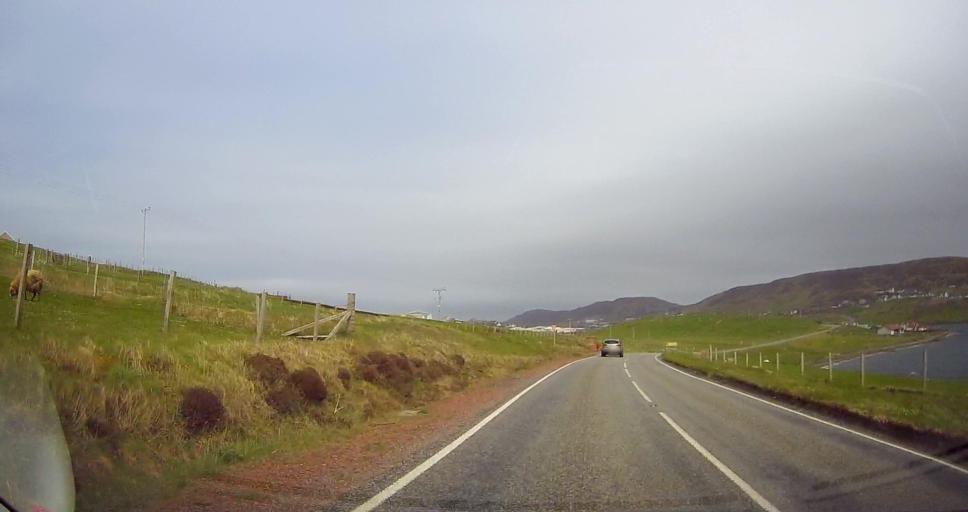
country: GB
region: Scotland
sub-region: Shetland Islands
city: Sandwick
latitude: 60.1243
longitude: -1.2854
